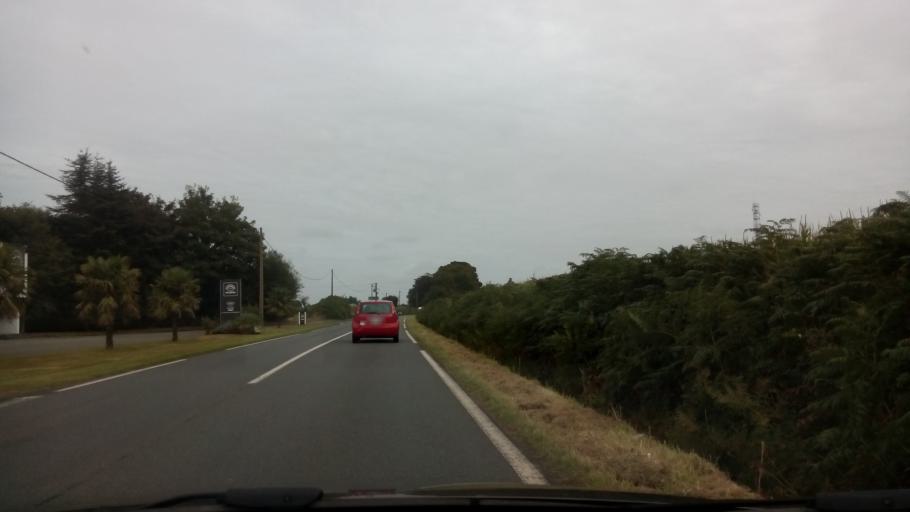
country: FR
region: Brittany
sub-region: Departement des Cotes-d'Armor
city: Ploumilliau
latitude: 48.7131
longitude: -3.4981
